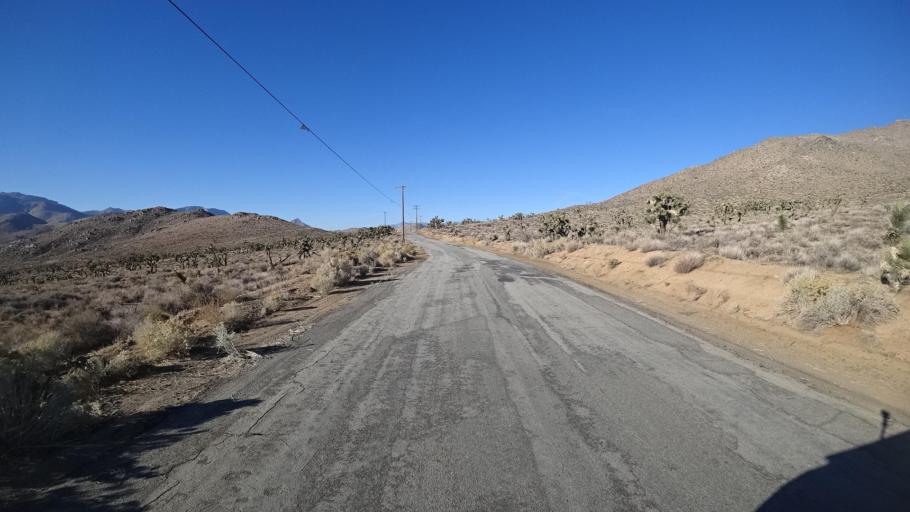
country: US
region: California
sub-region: Kern County
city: Weldon
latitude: 35.5268
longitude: -118.1999
